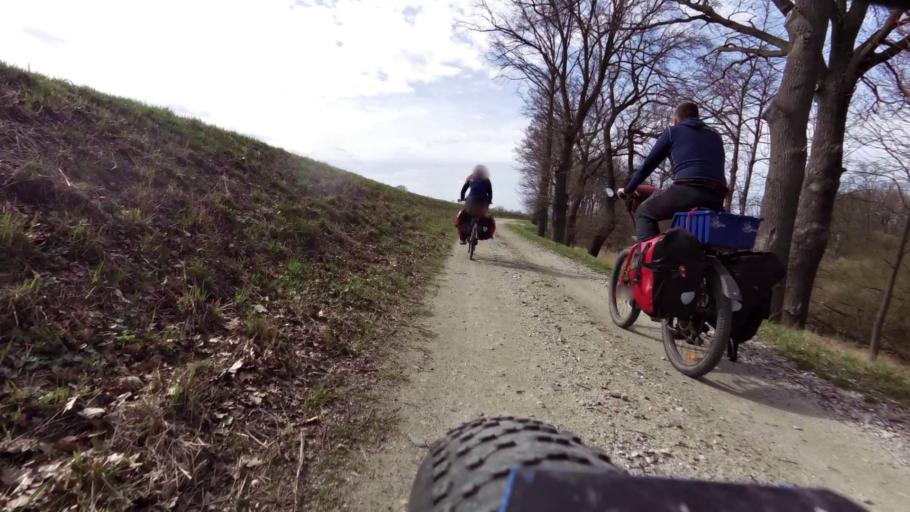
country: PL
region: Lubusz
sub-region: Powiat slubicki
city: Gorzyca
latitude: 52.5080
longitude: 14.6199
